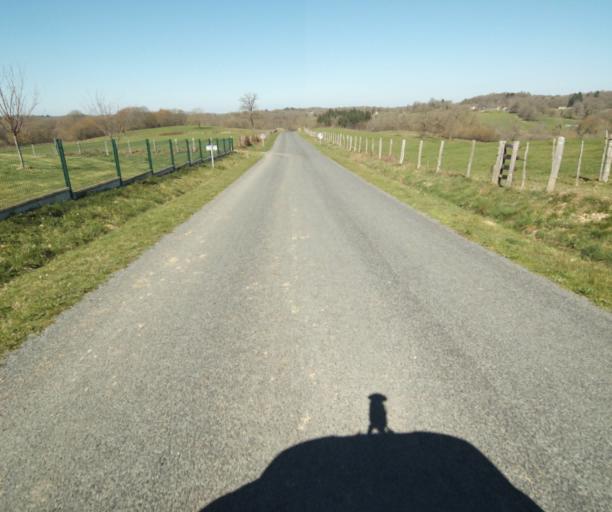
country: FR
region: Limousin
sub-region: Departement de la Correze
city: Saint-Clement
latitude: 45.3272
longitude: 1.6605
